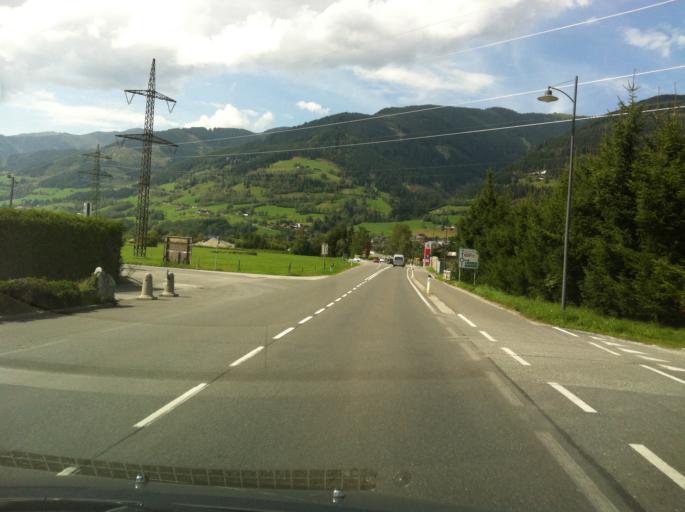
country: AT
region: Salzburg
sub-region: Politischer Bezirk Zell am See
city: Kaprun
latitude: 47.2808
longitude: 12.7551
